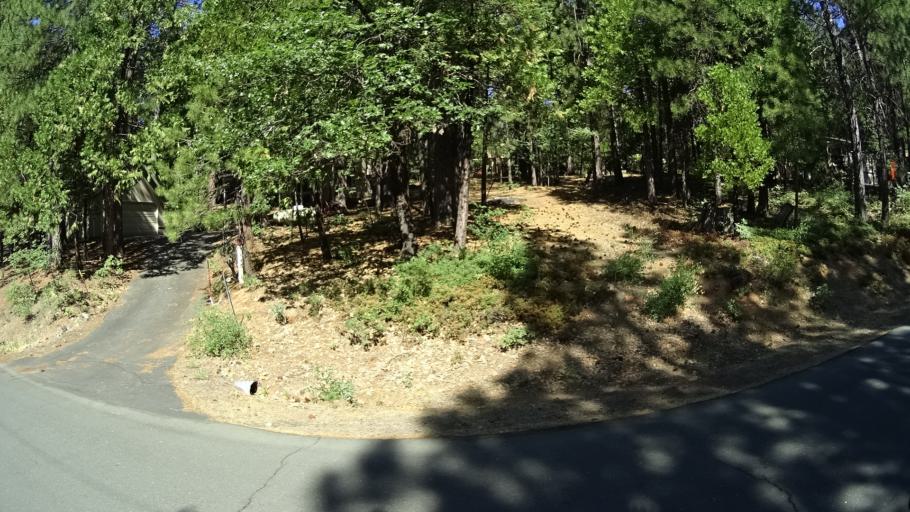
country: US
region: California
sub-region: Calaveras County
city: Arnold
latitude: 38.2532
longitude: -120.3646
